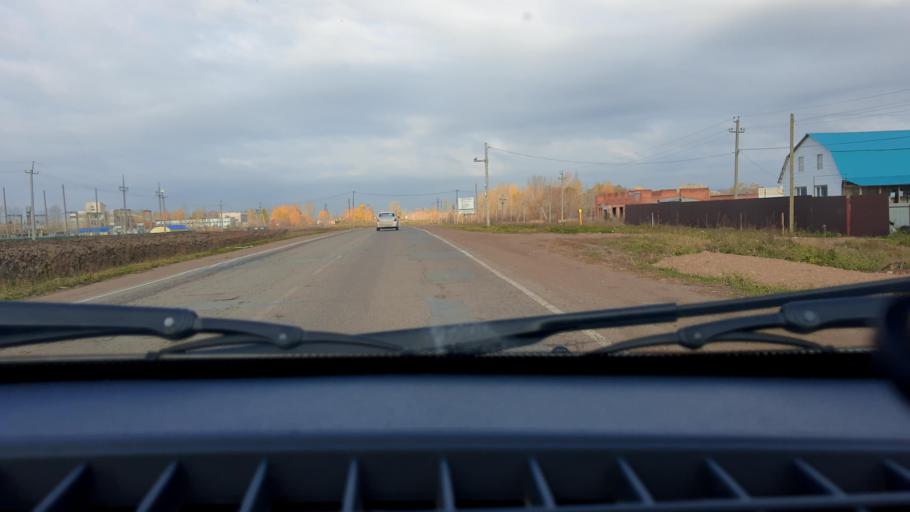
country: RU
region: Bashkortostan
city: Kabakovo
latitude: 54.5440
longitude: 56.1195
